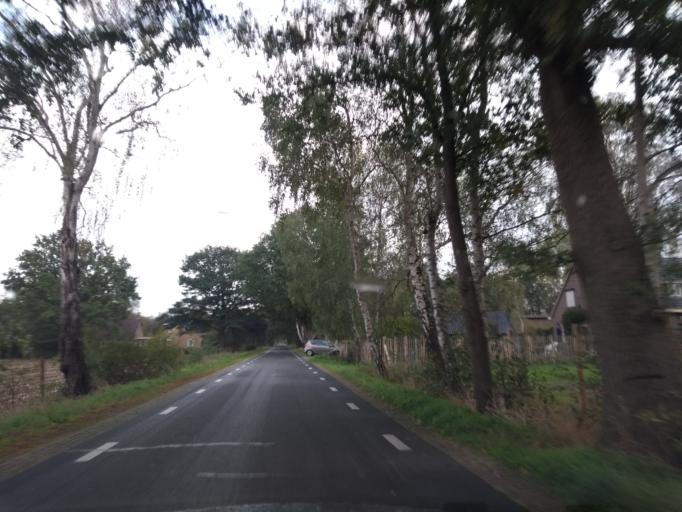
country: NL
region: Gelderland
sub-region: Gemeente Bronckhorst
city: Zelhem
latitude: 52.0306
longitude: 6.3511
